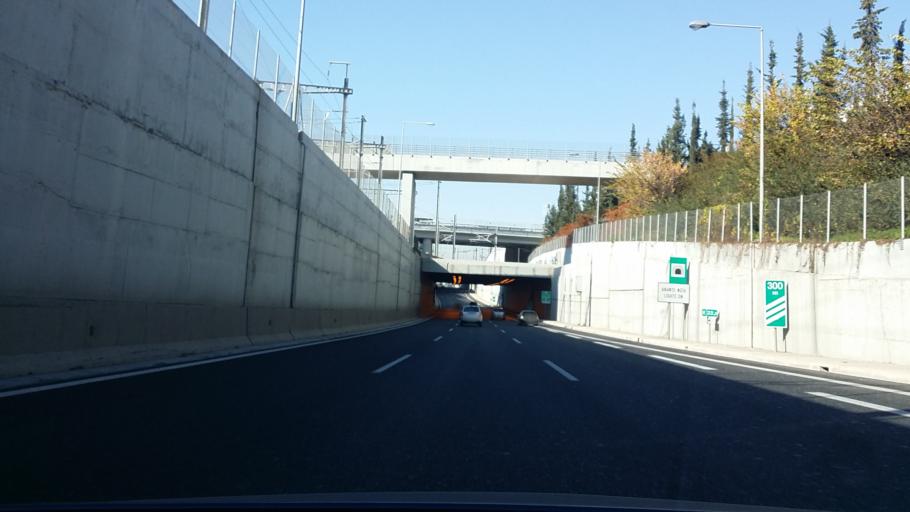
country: GR
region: Attica
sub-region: Nomarchia Anatolikis Attikis
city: Acharnes
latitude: 38.0649
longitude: 23.7410
